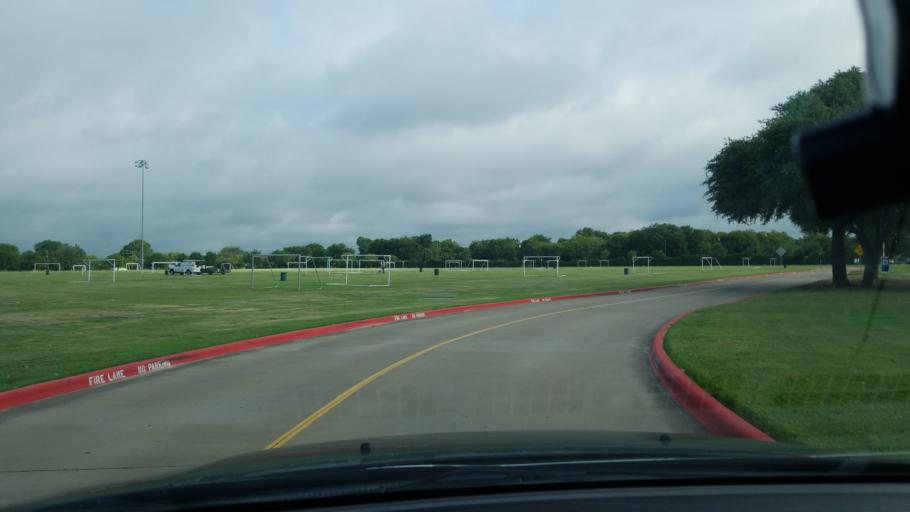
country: US
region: Texas
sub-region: Dallas County
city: Mesquite
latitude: 32.8133
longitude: -96.6622
